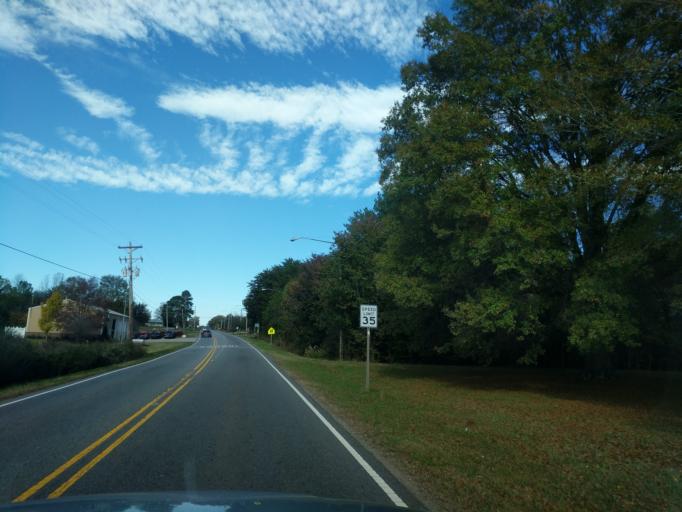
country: US
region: North Carolina
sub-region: Catawba County
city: Newton
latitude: 35.6345
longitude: -81.2673
